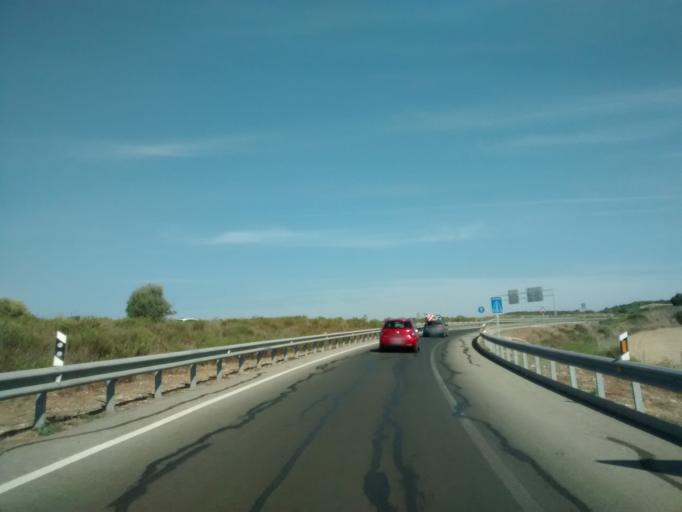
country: ES
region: Andalusia
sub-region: Provincia de Cadiz
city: Conil de la Frontera
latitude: 36.2935
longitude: -6.0563
